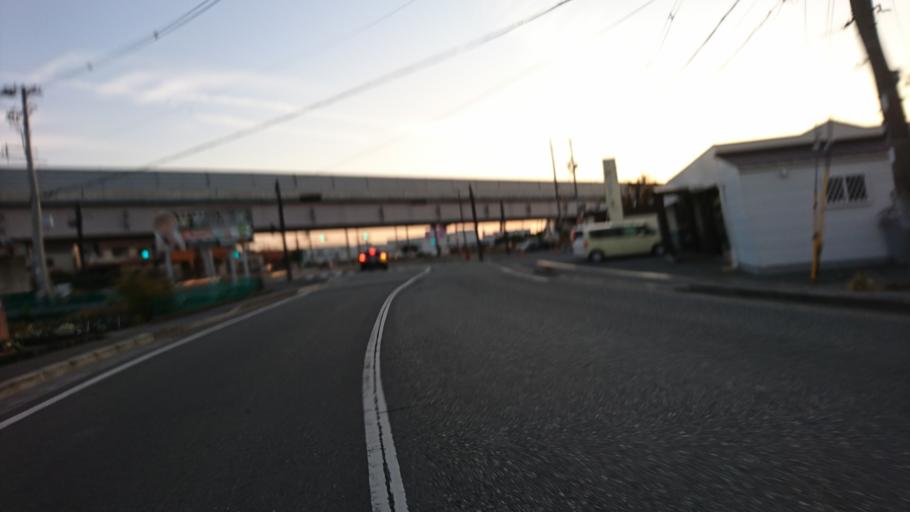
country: JP
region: Hyogo
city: Kakogawacho-honmachi
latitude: 34.7650
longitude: 134.8634
